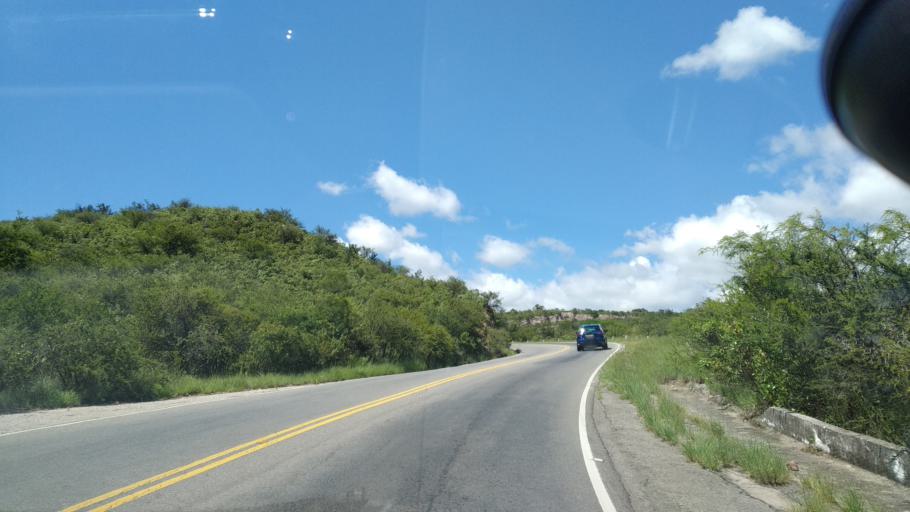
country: AR
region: Cordoba
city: Villa Cura Brochero
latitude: -31.6956
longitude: -65.0518
